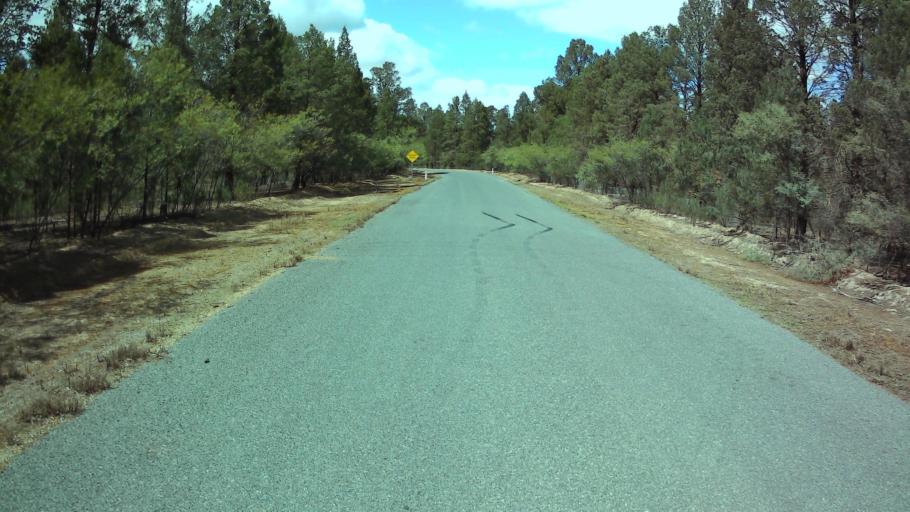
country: AU
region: New South Wales
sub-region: Weddin
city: Grenfell
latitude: -33.9082
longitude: 147.9194
